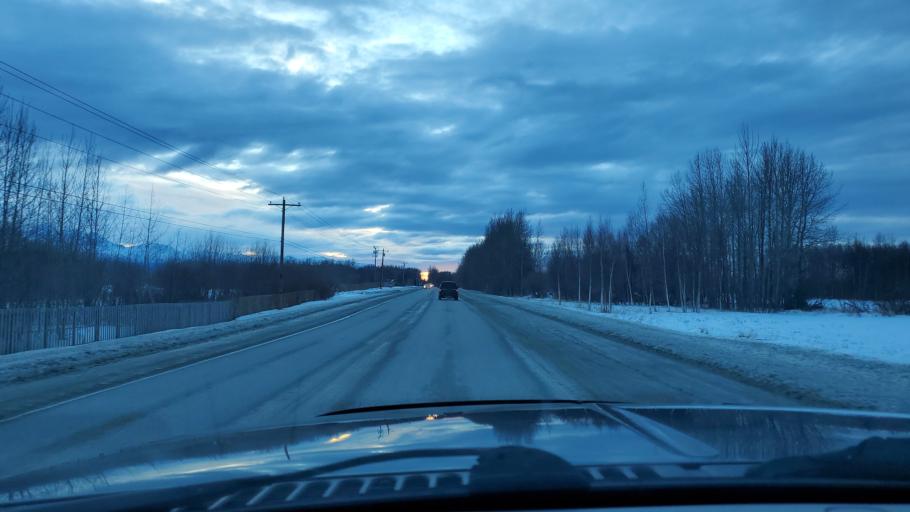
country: US
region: Alaska
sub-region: Matanuska-Susitna Borough
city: Farm Loop
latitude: 61.6619
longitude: -149.0906
